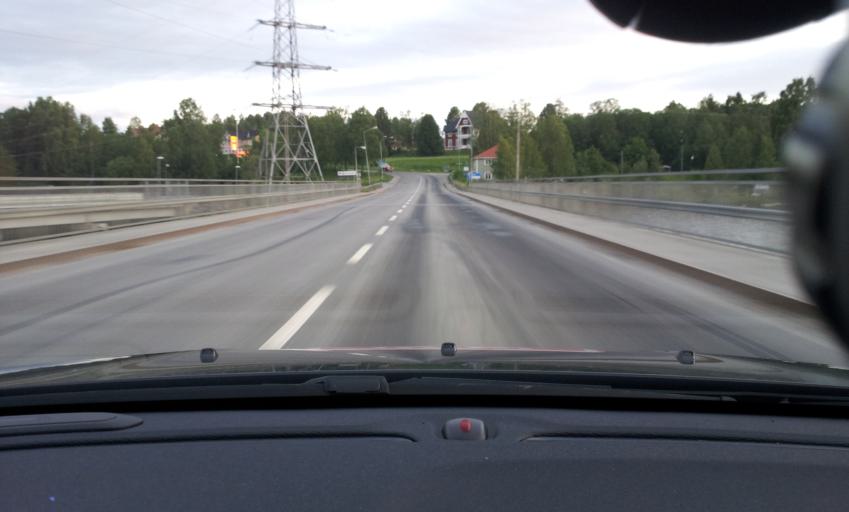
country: SE
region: Jaemtland
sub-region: Ragunda Kommun
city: Hammarstrand
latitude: 63.1139
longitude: 16.3550
